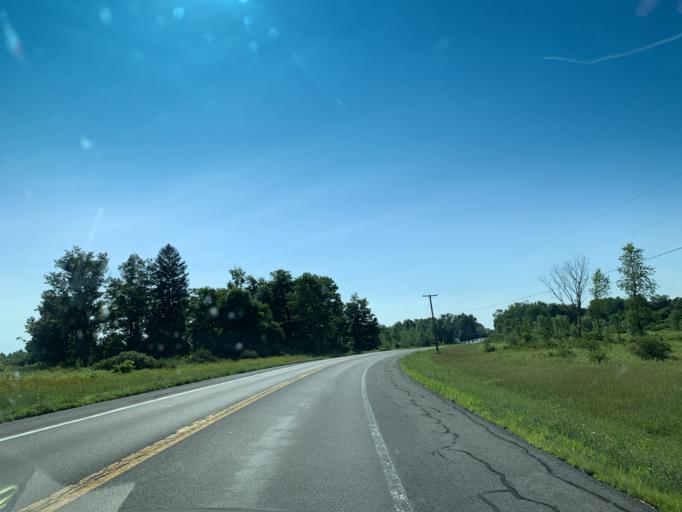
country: US
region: New York
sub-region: Oneida County
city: Sherrill
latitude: 43.1344
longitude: -75.6053
